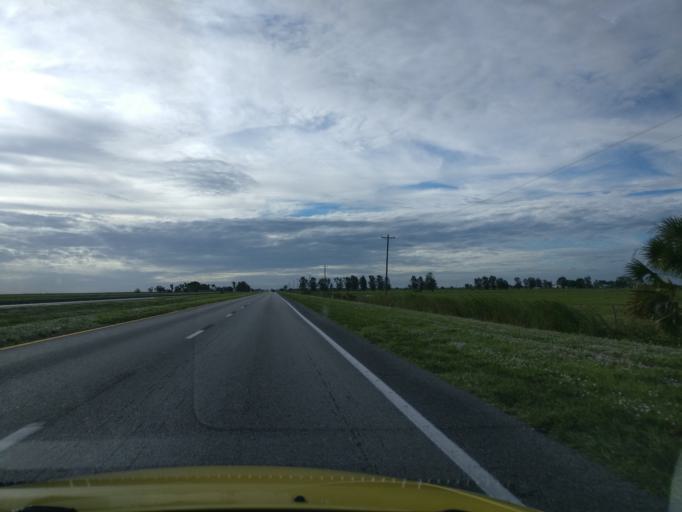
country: US
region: Florida
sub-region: Hendry County
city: Harlem
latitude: 26.7544
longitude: -81.0082
